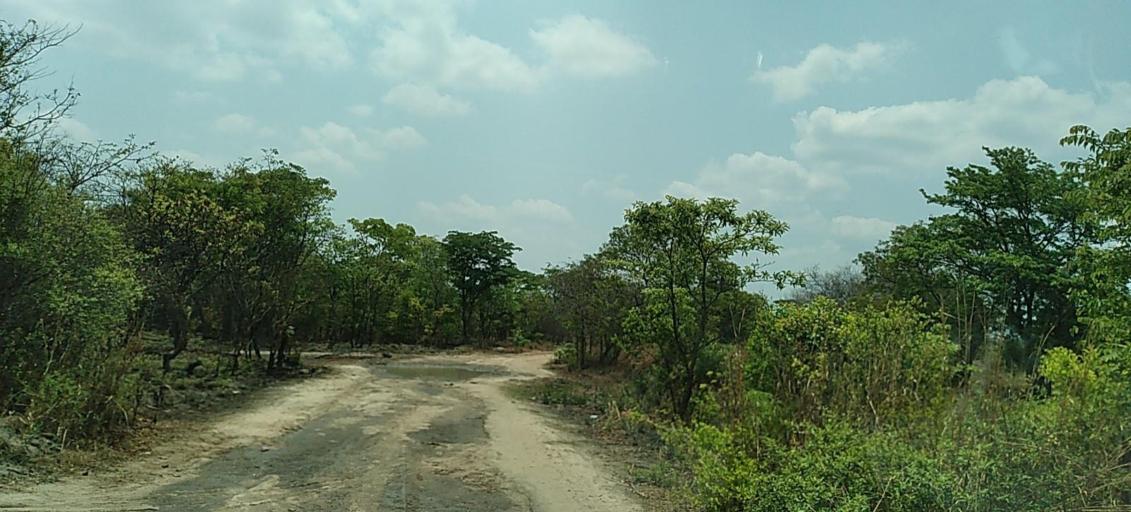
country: ZM
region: Copperbelt
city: Luanshya
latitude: -13.0964
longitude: 28.2907
